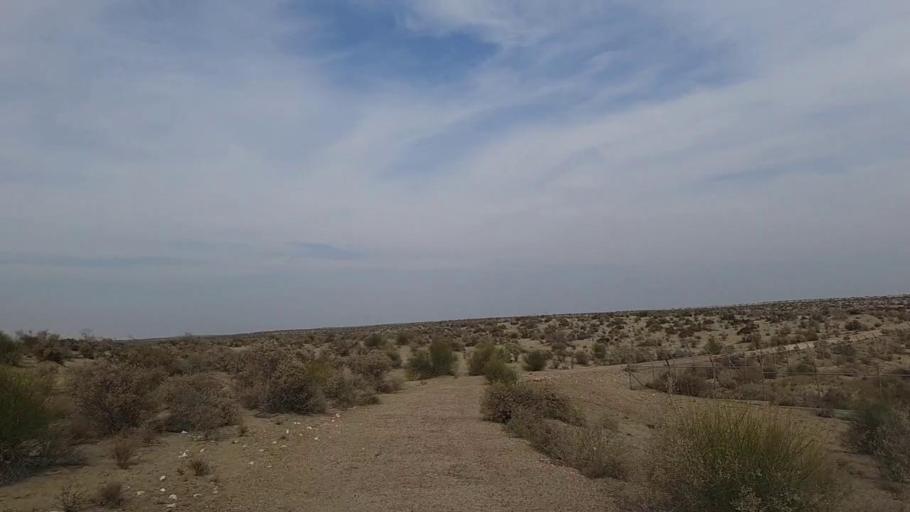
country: PK
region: Sindh
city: Jam Sahib
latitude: 26.4582
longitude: 68.6522
